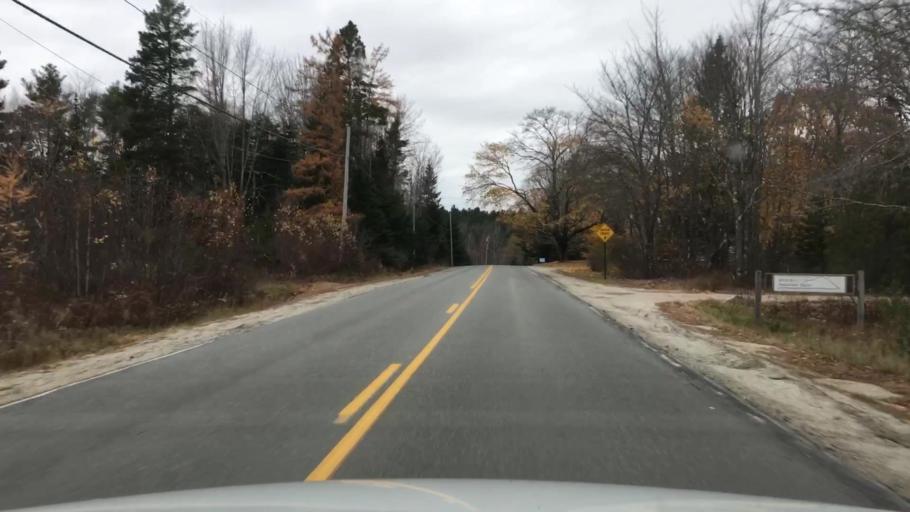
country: US
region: Maine
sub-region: Hancock County
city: Penobscot
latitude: 44.4214
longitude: -68.6196
